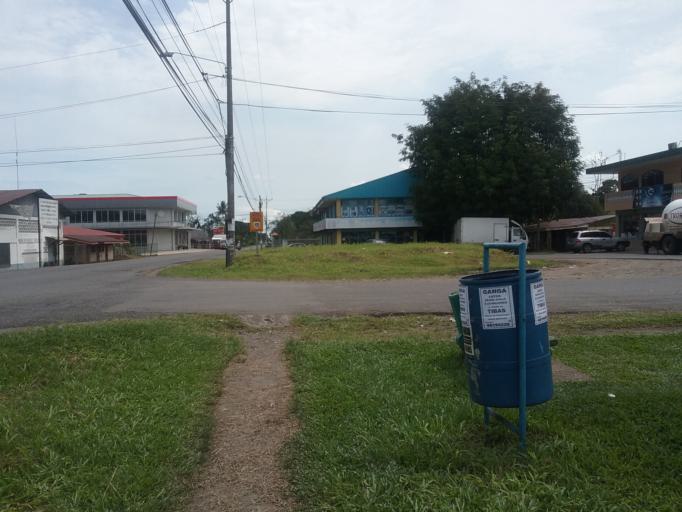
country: CR
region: Limon
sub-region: Canton de Pococi
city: Guapiles
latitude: 10.3203
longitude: -83.8865
